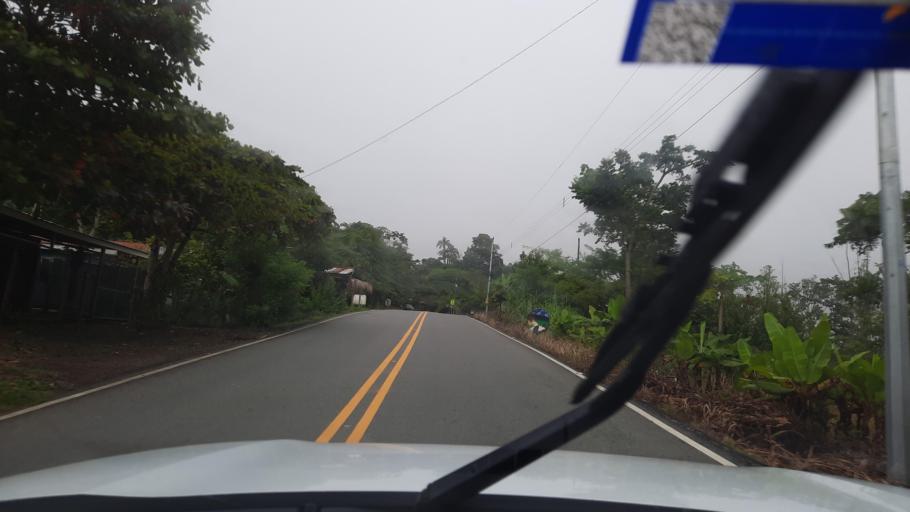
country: CR
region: Puntarenas
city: San Vito
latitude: 8.9351
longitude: -83.0953
